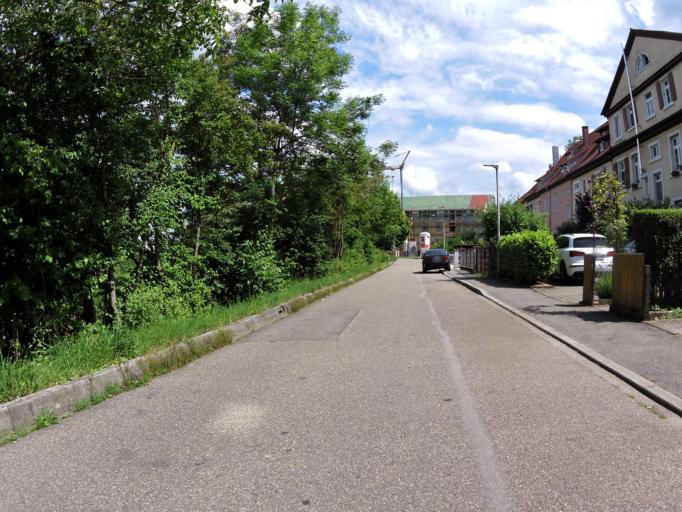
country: DE
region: Baden-Wuerttemberg
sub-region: Freiburg Region
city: Lahr
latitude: 48.3382
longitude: 7.8531
